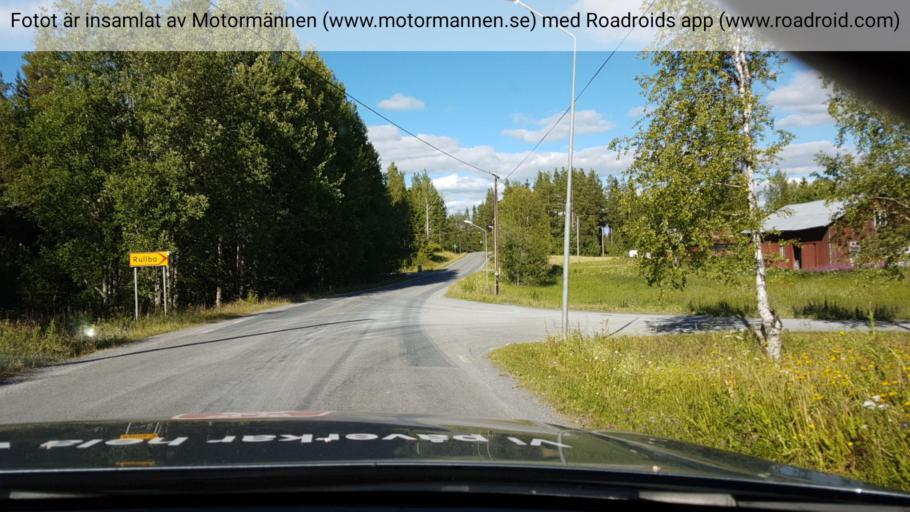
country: SE
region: Jaemtland
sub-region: Krokoms Kommun
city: Valla
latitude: 63.2826
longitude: 13.7678
